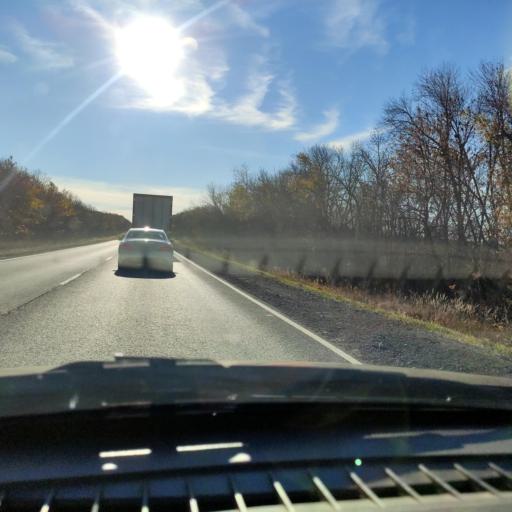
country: RU
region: Samara
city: Zhigulevsk
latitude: 53.2959
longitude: 49.3366
